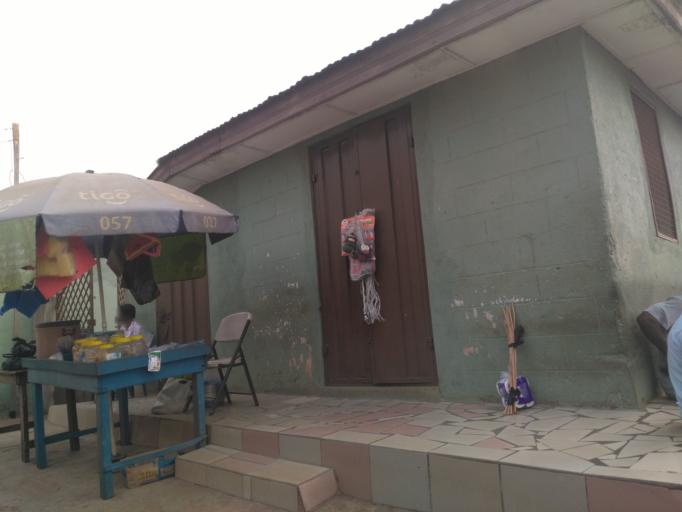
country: GH
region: Ashanti
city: Kumasi
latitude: 6.6780
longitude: -1.5926
